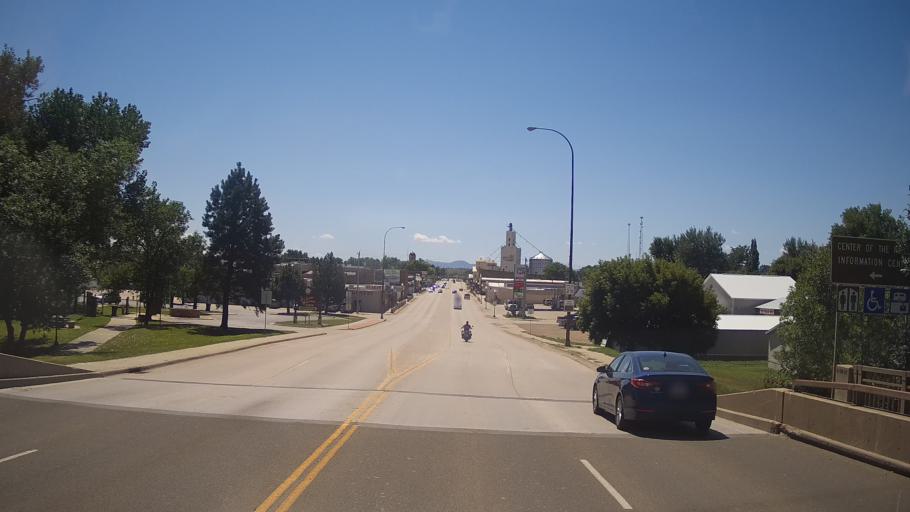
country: US
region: South Dakota
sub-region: Butte County
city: Belle Fourche
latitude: 44.6748
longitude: -103.8536
